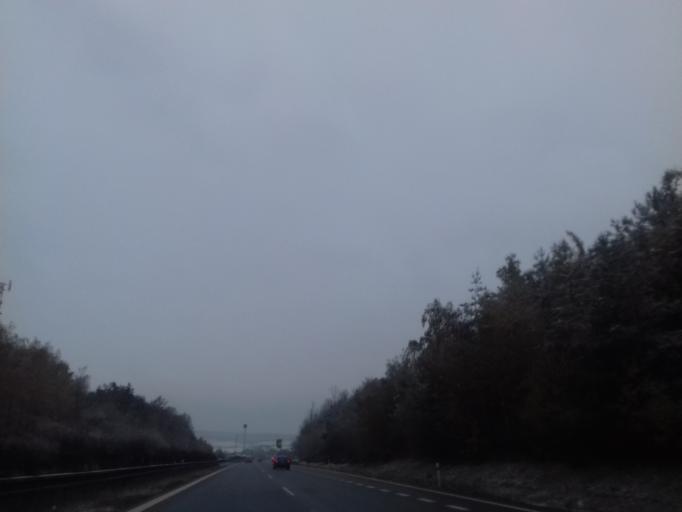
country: CZ
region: Central Bohemia
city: Zebrak
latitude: 49.8563
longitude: 13.8757
